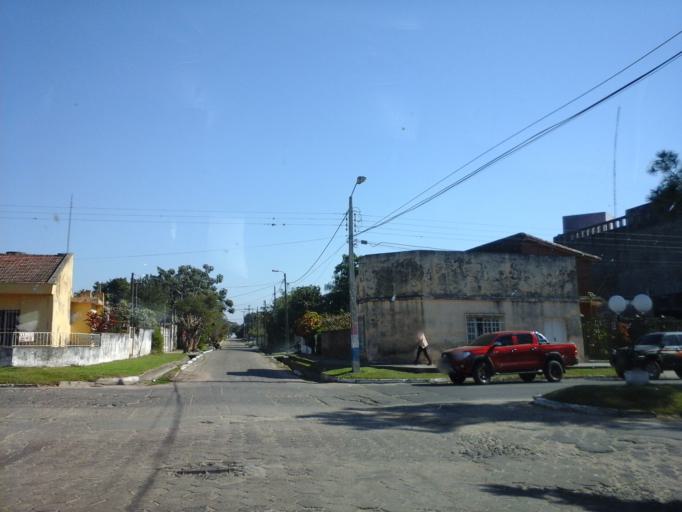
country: PY
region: Neembucu
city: Pilar
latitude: -26.8596
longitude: -58.3065
